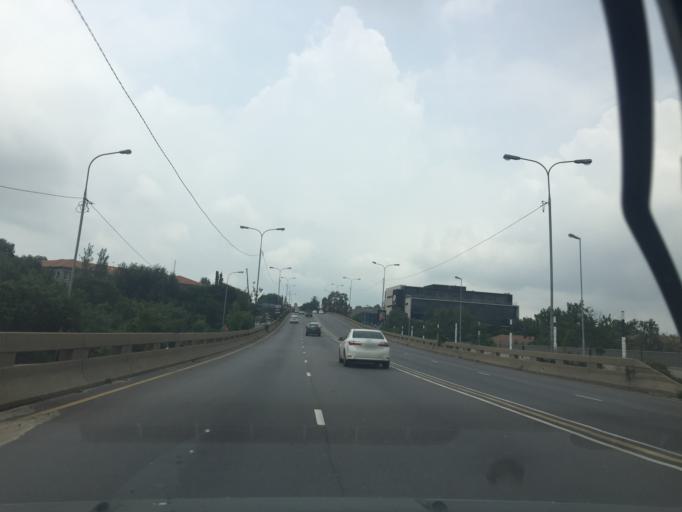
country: ZA
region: Gauteng
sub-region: City of Johannesburg Metropolitan Municipality
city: Modderfontein
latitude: -26.1054
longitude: 28.0735
